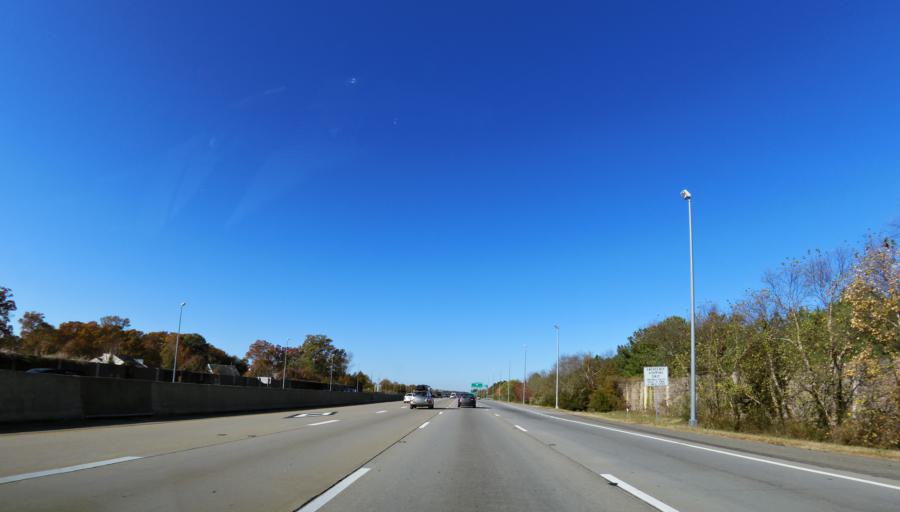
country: US
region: Virginia
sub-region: York County
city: Yorktown
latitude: 37.1141
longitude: -76.4893
